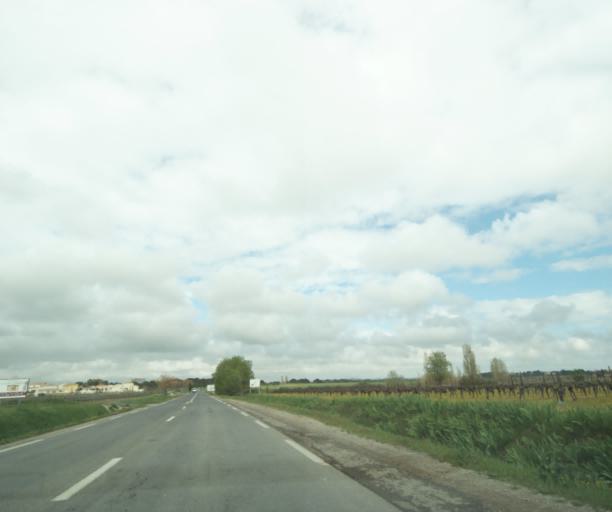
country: FR
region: Languedoc-Roussillon
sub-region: Departement de l'Herault
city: Pignan
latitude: 43.5762
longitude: 3.7505
